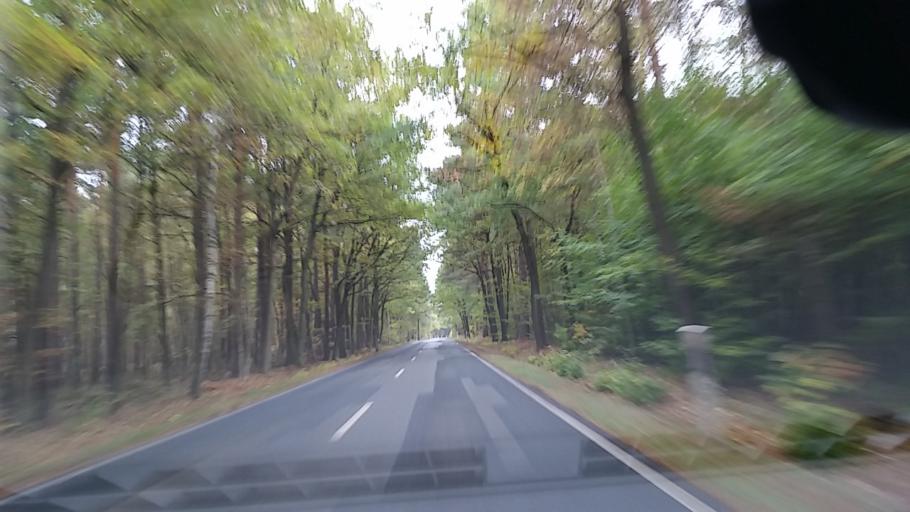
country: DE
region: Lower Saxony
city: Tulau
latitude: 52.6296
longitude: 10.8140
